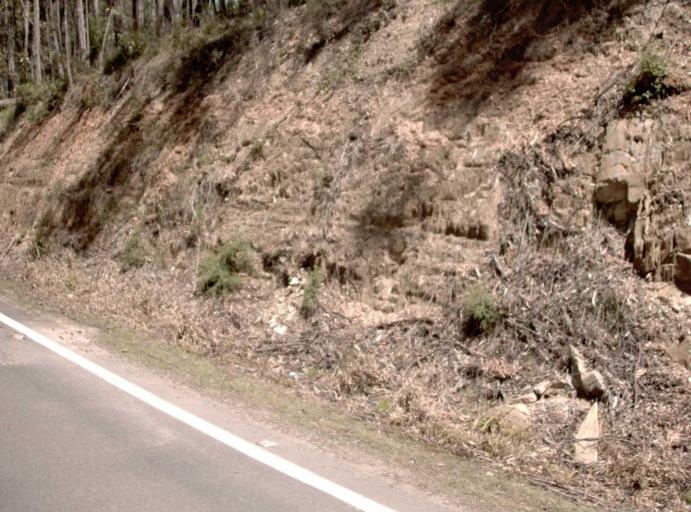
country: AU
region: New South Wales
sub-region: Bombala
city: Bombala
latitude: -37.5866
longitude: 148.9533
